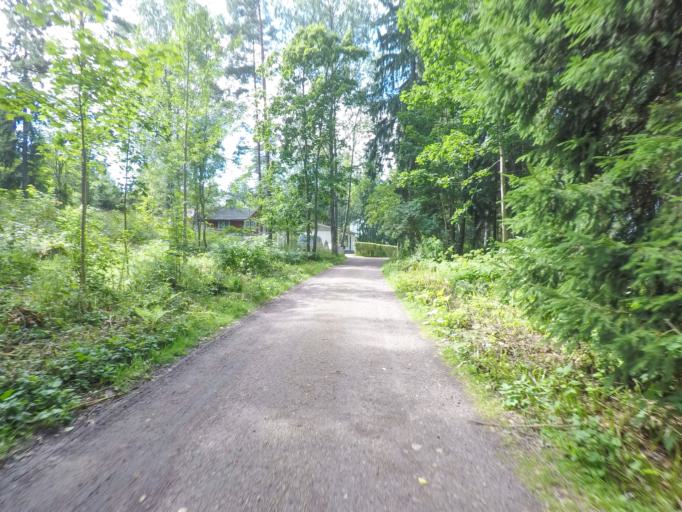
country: FI
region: Uusimaa
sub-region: Helsinki
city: Vantaa
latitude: 60.1677
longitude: 25.0780
